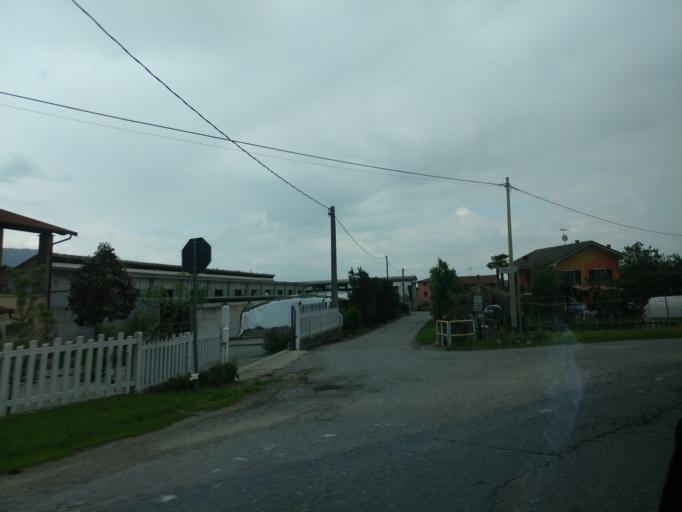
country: IT
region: Piedmont
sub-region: Provincia di Cuneo
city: Revello
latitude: 44.6699
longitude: 7.3989
